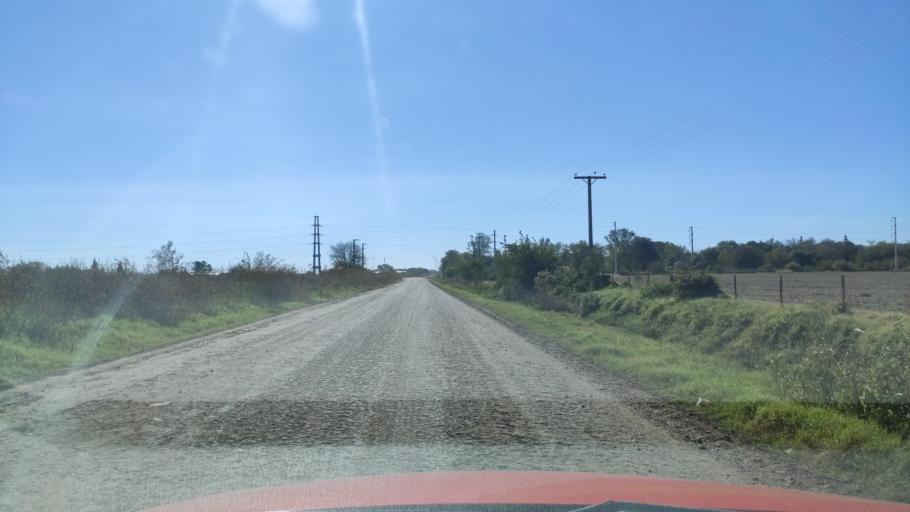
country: AR
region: Cordoba
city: Leones
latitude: -32.6648
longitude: -62.3115
